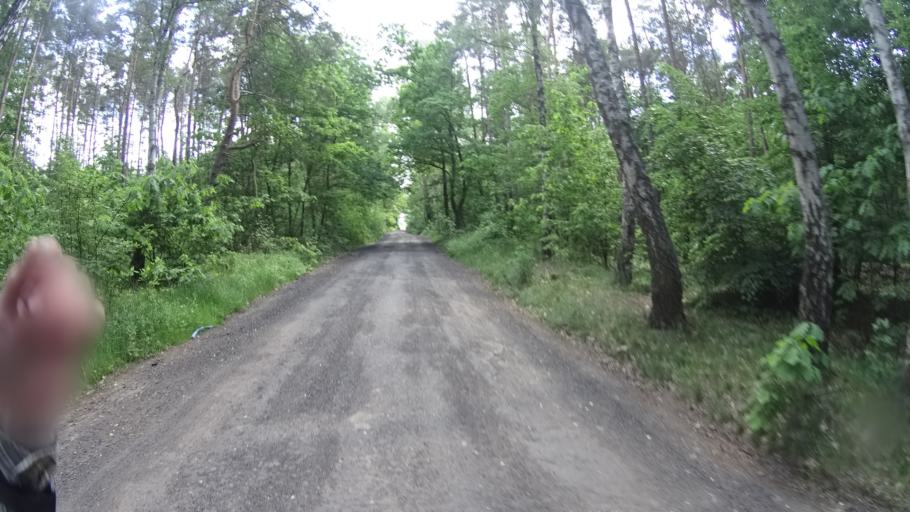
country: PL
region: Masovian Voivodeship
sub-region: Powiat pruszkowski
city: Nadarzyn
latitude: 52.0650
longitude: 20.8207
